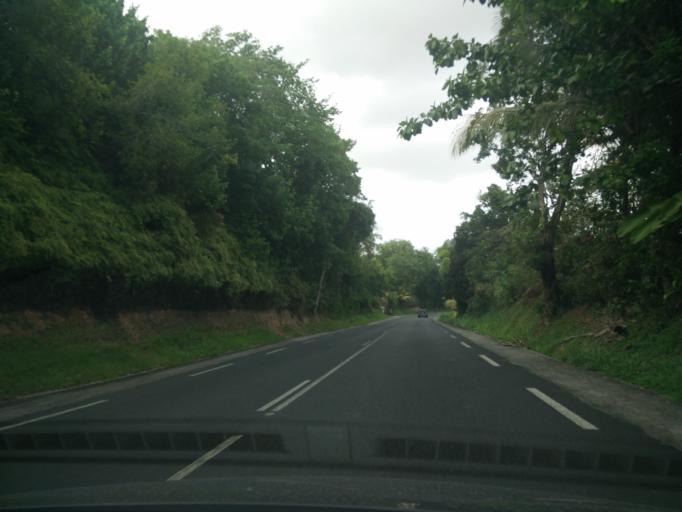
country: GP
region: Guadeloupe
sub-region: Guadeloupe
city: Petit-Bourg
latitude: 16.2035
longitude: -61.6356
